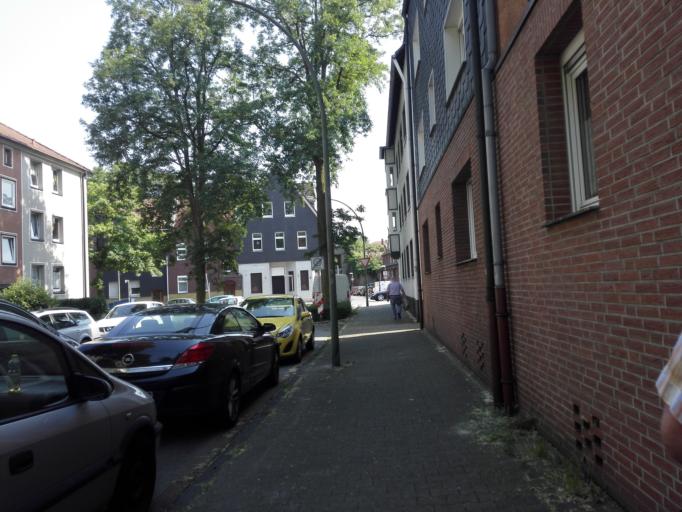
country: DE
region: North Rhine-Westphalia
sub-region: Regierungsbezirk Munster
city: Gladbeck
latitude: 51.5288
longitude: 7.0254
